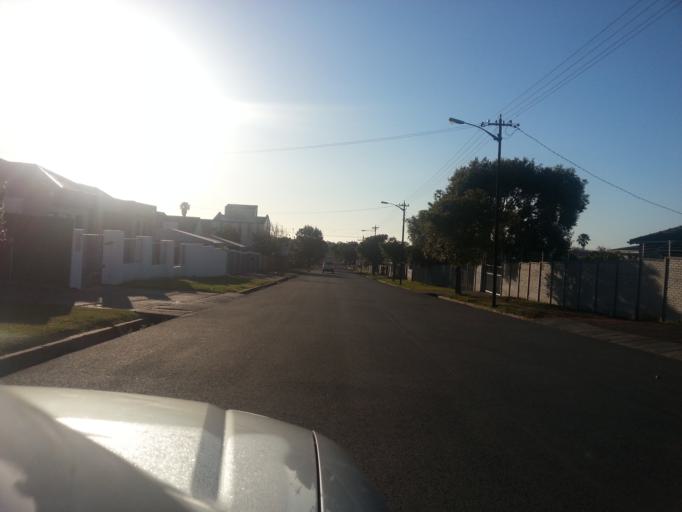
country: ZA
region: Eastern Cape
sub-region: Buffalo City Metropolitan Municipality
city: East London
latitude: -32.9848
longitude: 27.9221
